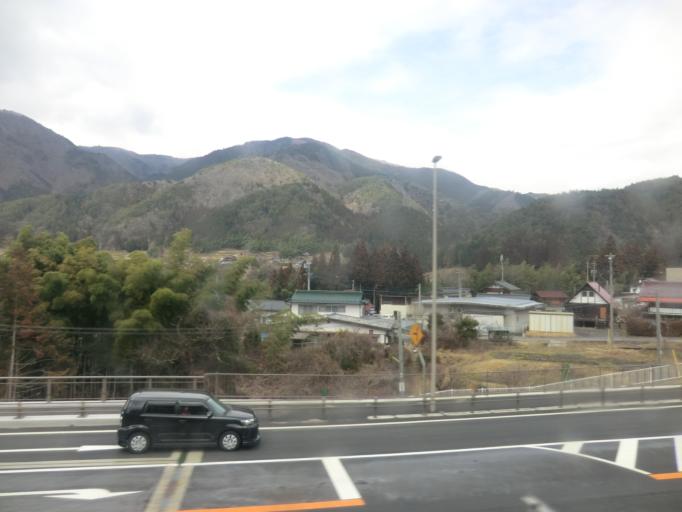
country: JP
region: Nagano
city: Iida
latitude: 35.6850
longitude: 137.6652
